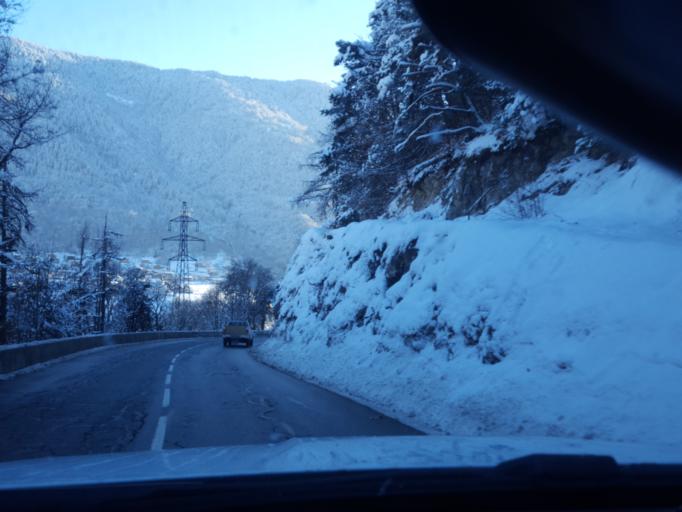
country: FR
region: Rhone-Alpes
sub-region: Departement de la Savoie
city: Salins-les-Thermes
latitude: 45.4703
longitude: 6.5235
